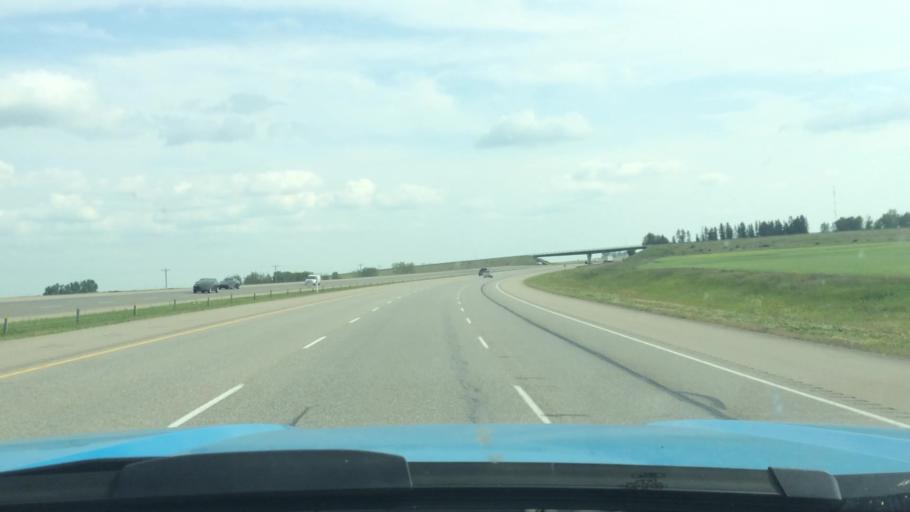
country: CA
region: Alberta
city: Crossfield
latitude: 51.4359
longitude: -114.0034
